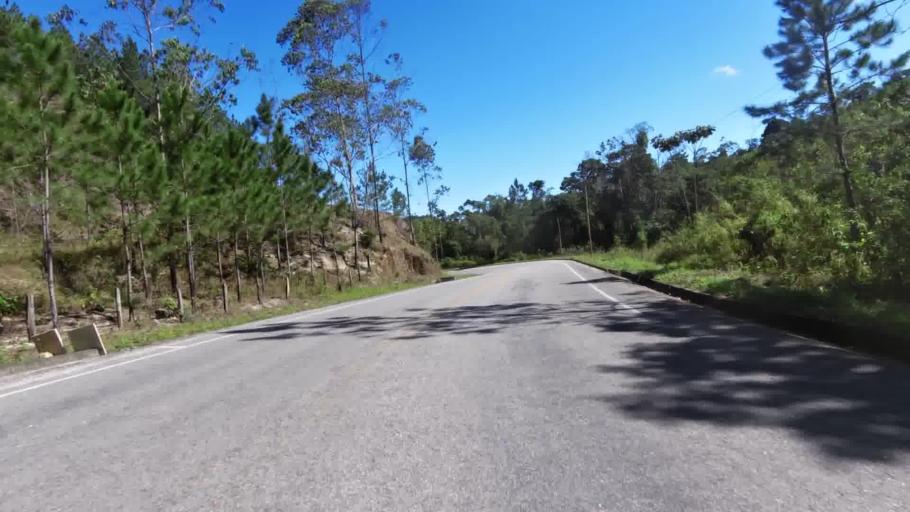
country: BR
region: Espirito Santo
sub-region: Vargem Alta
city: Vargem Alta
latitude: -20.6848
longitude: -40.9465
